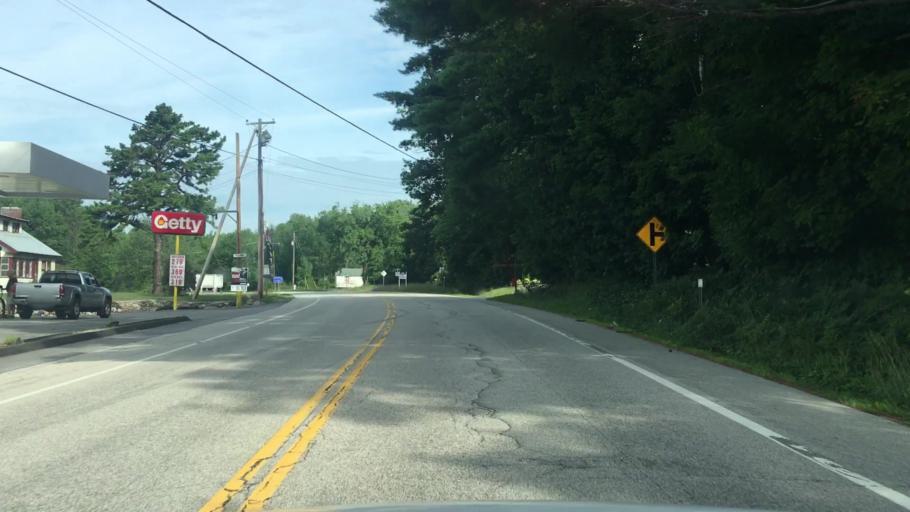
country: US
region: New Hampshire
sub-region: Carroll County
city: Effingham
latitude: 43.7961
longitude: -70.9980
